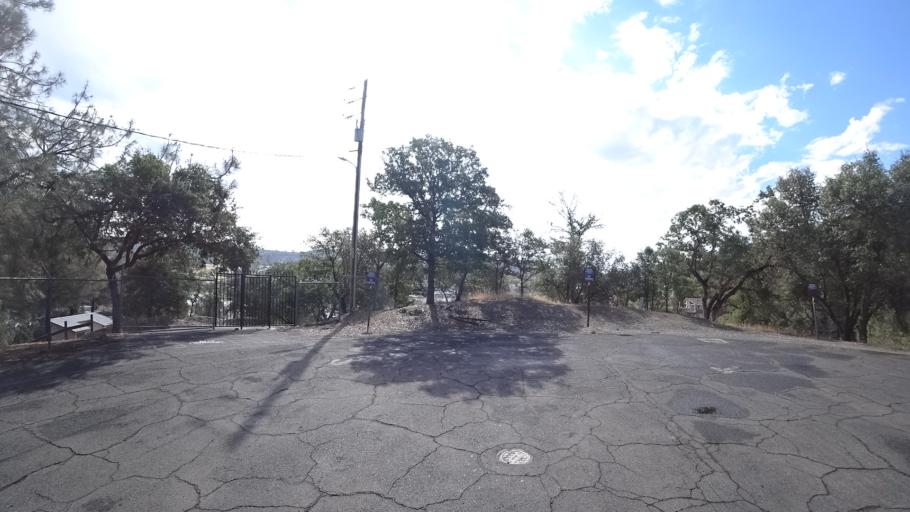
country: US
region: California
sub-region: Calaveras County
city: Copperopolis
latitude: 37.9118
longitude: -120.6047
